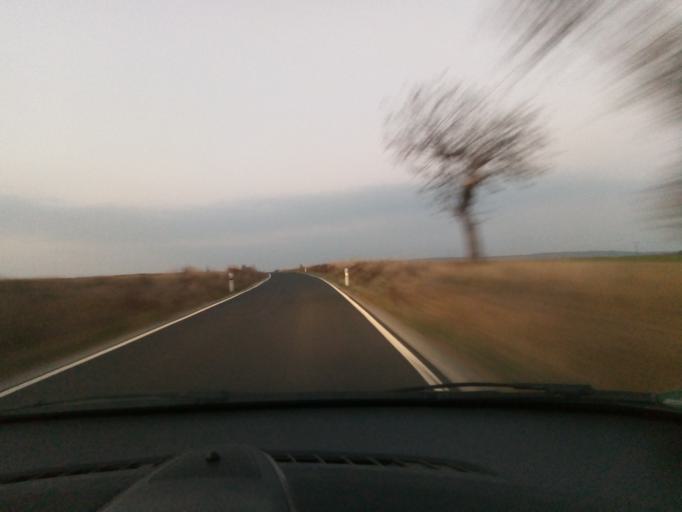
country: DE
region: Bavaria
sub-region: Regierungsbezirk Unterfranken
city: Oberschwarzach
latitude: 49.8285
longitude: 10.4018
